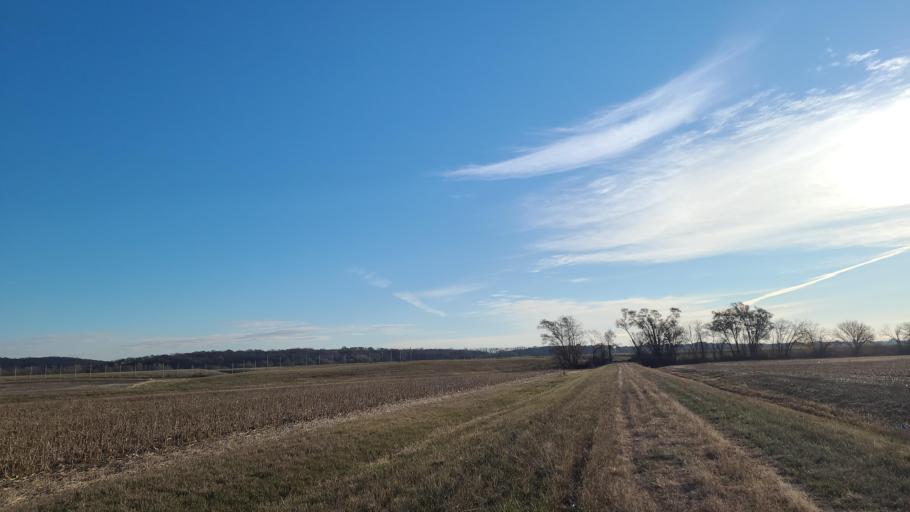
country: US
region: Kansas
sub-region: Douglas County
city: Lawrence
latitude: 39.0151
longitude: -95.2225
